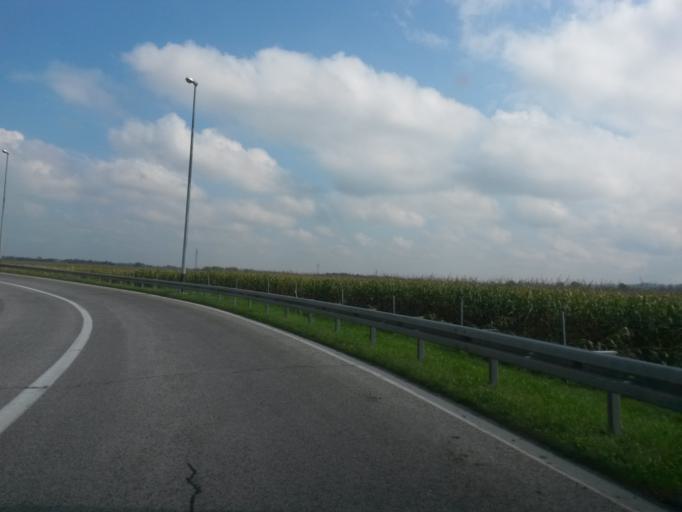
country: HR
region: Medimurska
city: Kursanec
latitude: 46.2595
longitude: 16.4016
